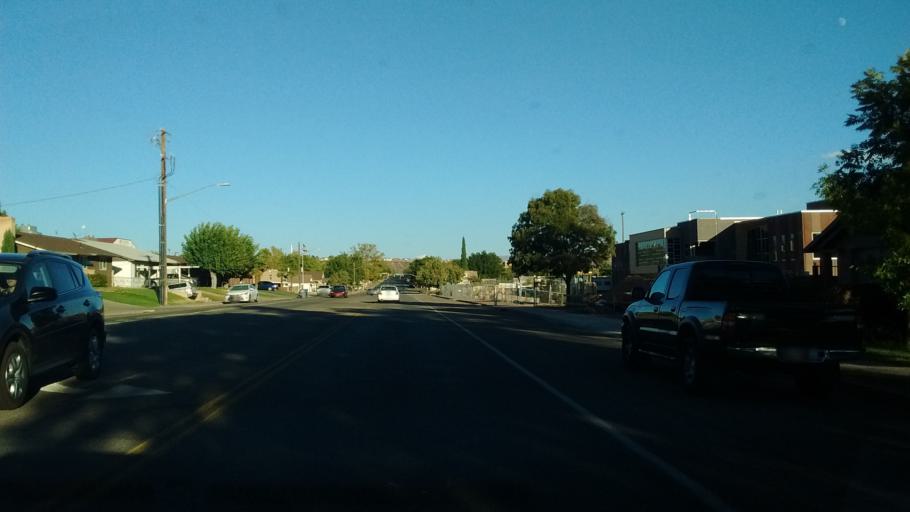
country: US
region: Utah
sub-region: Washington County
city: Saint George
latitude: 37.1065
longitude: -113.5786
